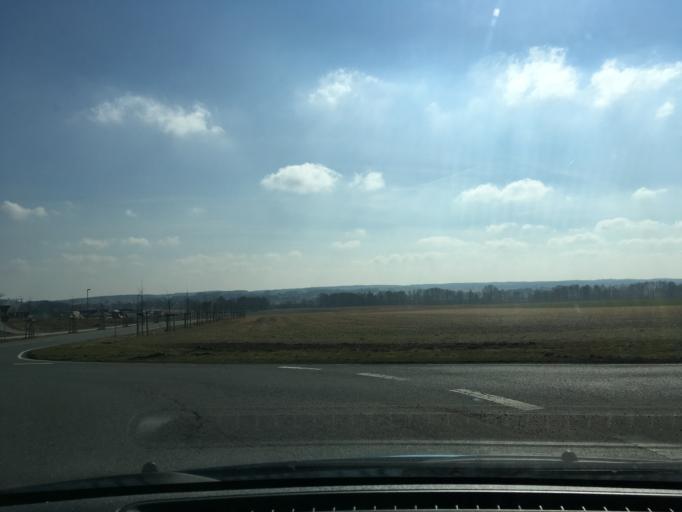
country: DE
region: Lower Saxony
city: Salzhausen
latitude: 53.2268
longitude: 10.1585
